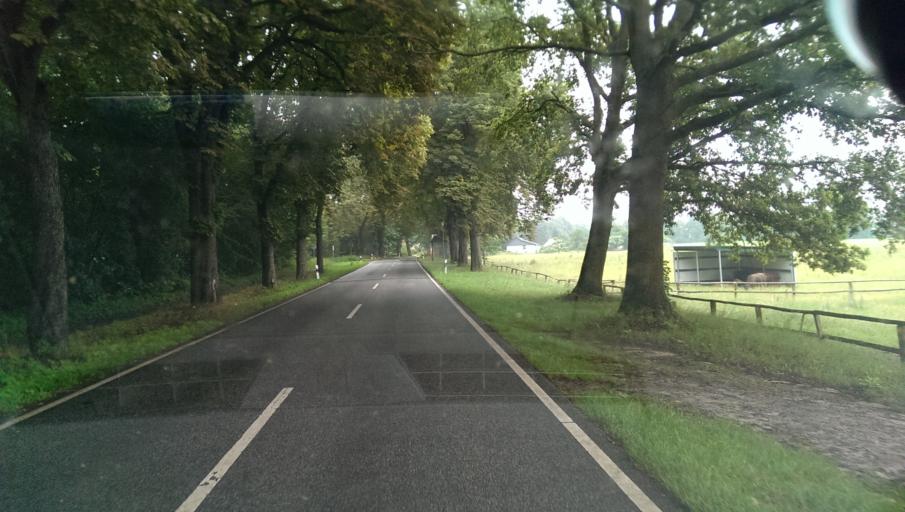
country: DE
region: Brandenburg
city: Pawesin
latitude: 52.5854
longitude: 12.7545
